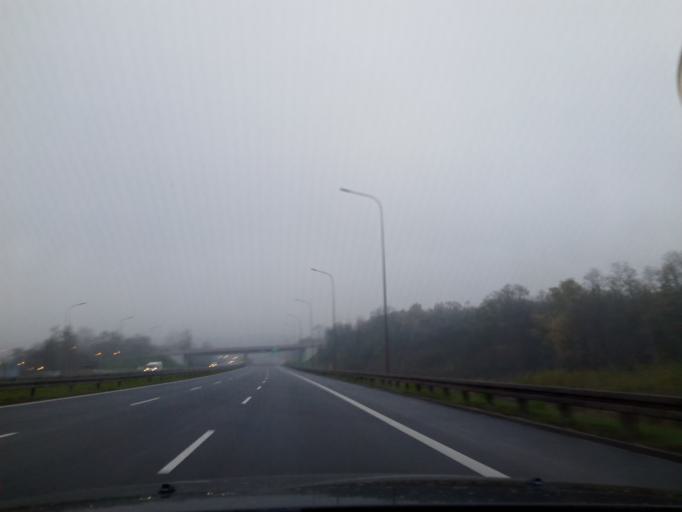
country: PL
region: Lesser Poland Voivodeship
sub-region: Powiat wielicki
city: Kokotow
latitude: 50.0545
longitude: 20.0753
